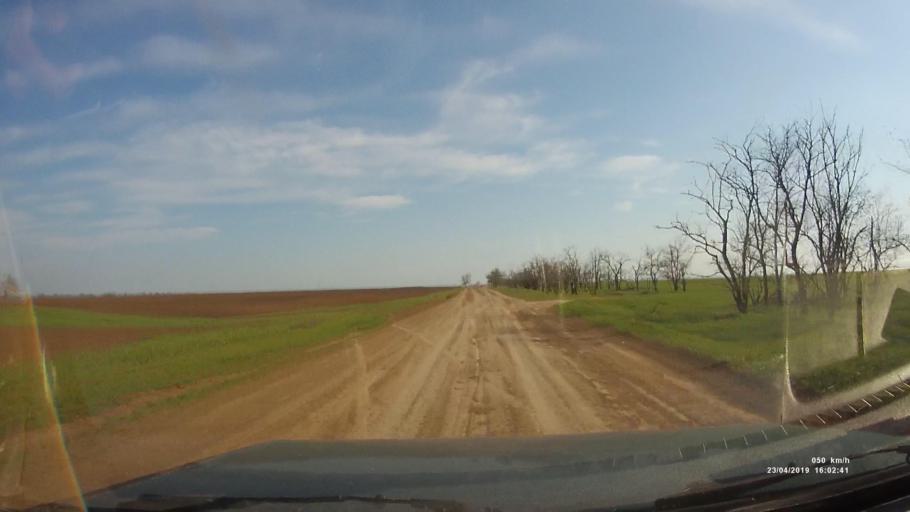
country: RU
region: Rostov
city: Remontnoye
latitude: 46.4925
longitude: 43.1071
